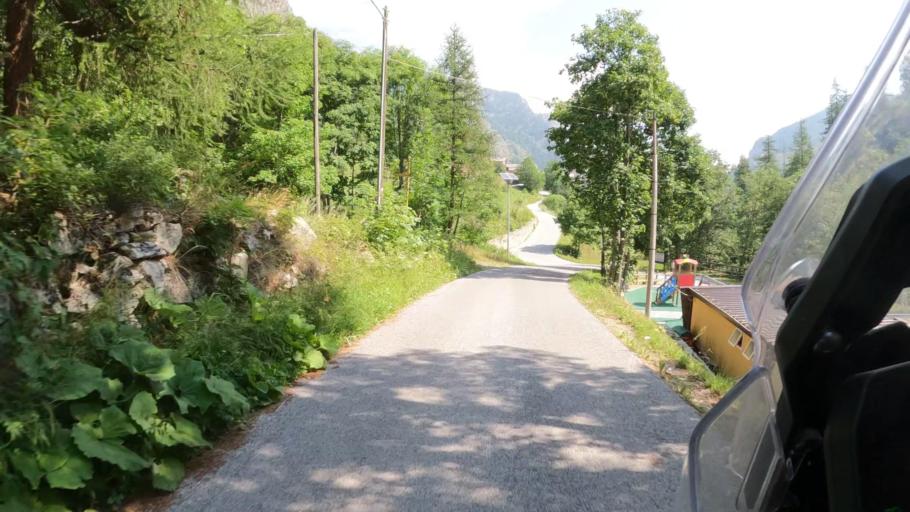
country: IT
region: Piedmont
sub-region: Provincia di Cuneo
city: Canosio
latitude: 44.4333
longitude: 7.0543
